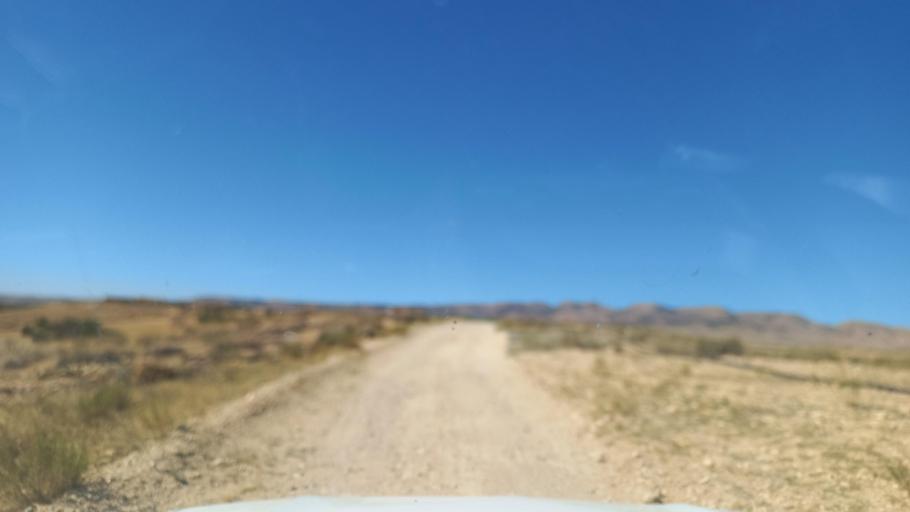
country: TN
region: Al Qasrayn
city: Sbiba
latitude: 35.3779
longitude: 9.0785
